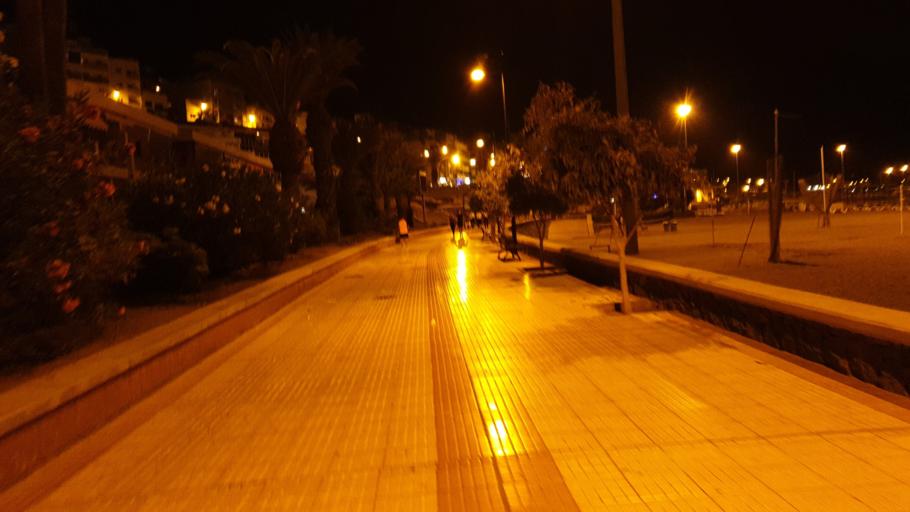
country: ES
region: Canary Islands
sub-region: Provincia de Santa Cruz de Tenerife
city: Playa de las Americas
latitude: 28.0531
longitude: -16.7245
